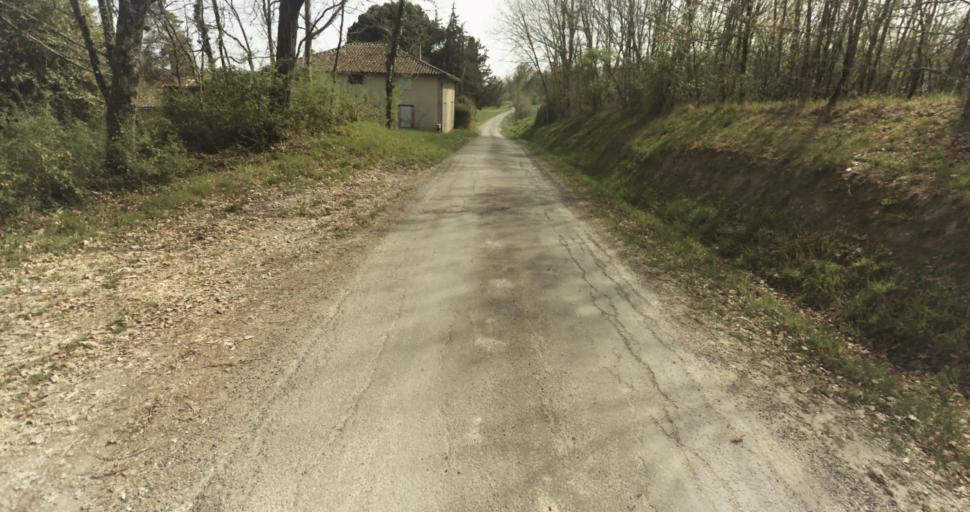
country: FR
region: Midi-Pyrenees
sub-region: Departement du Tarn-et-Garonne
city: Moissac
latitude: 44.1414
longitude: 1.1591
